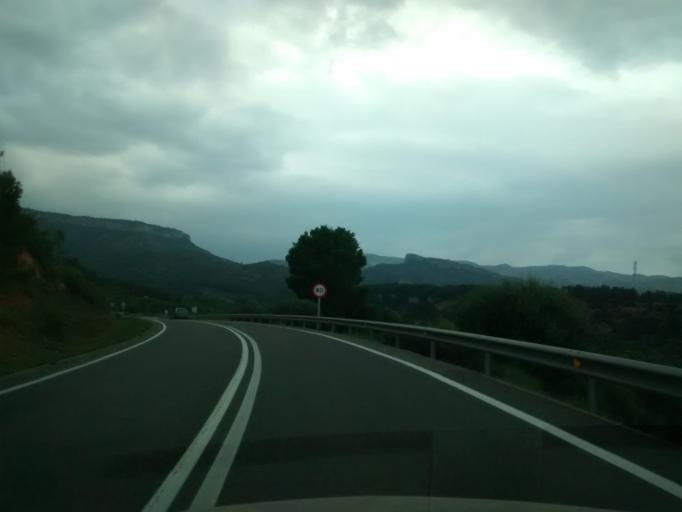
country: ES
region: Catalonia
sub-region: Provincia de Tarragona
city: Benifallet
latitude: 41.0154
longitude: 0.5047
